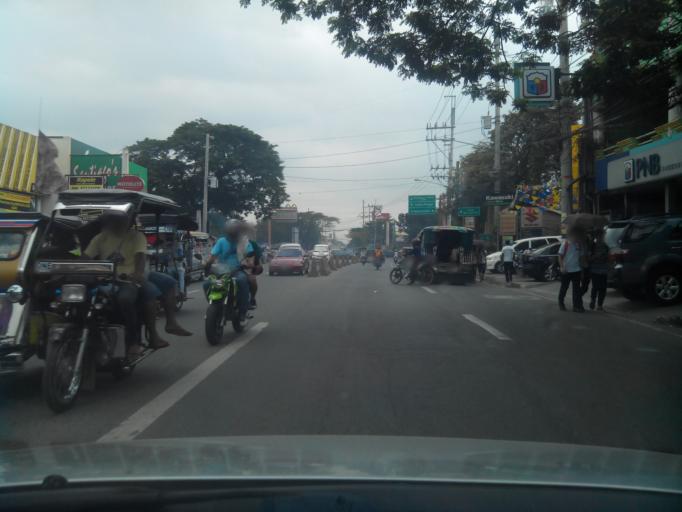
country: PH
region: Calabarzon
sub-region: Province of Rizal
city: Taytay
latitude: 14.5567
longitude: 121.1369
